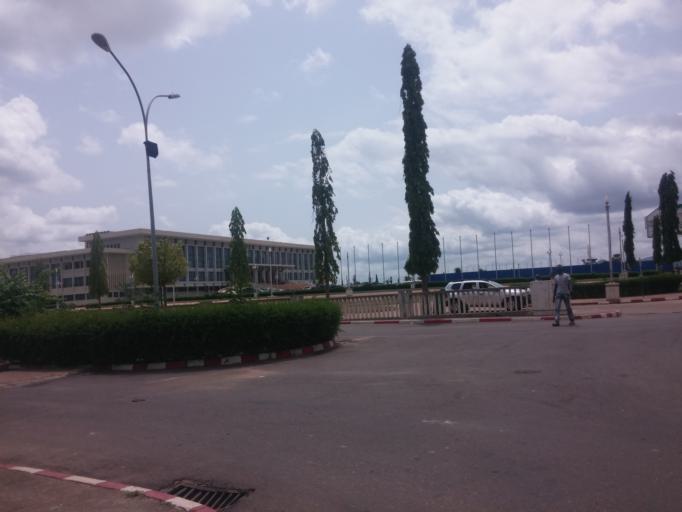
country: TG
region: Kara
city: Kara
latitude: 9.5592
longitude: 1.1822
